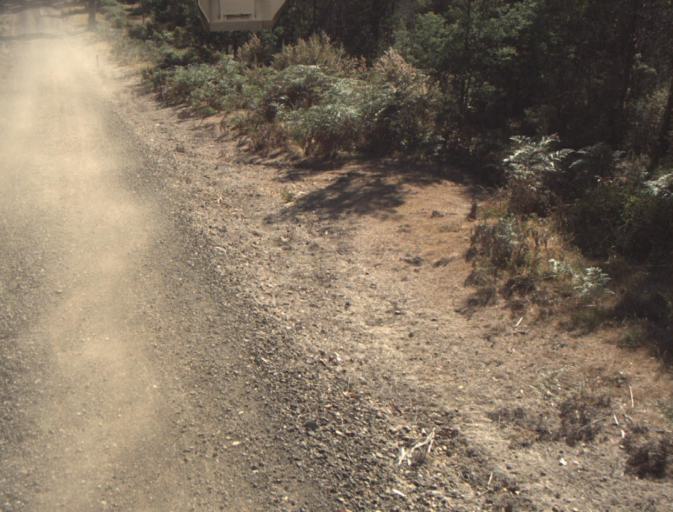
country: AU
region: Tasmania
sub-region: Dorset
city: Scottsdale
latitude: -41.2721
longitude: 147.3754
